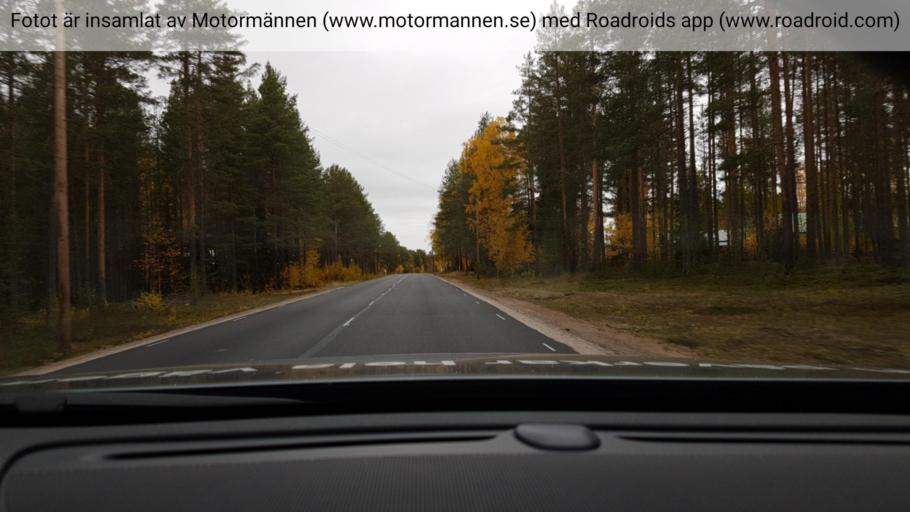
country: SE
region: Norrbotten
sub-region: Overkalix Kommun
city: OEverkalix
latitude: 66.4276
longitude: 22.7958
